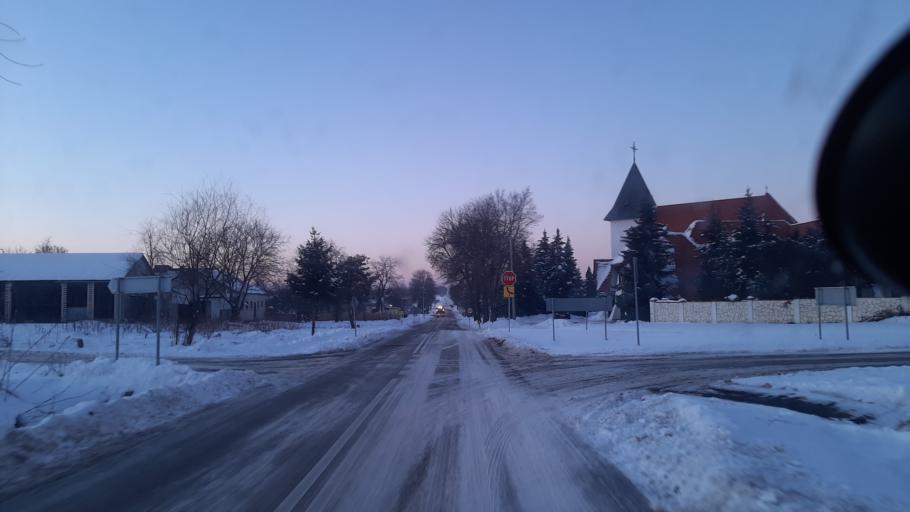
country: PL
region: Lublin Voivodeship
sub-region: Powiat lubelski
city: Niemce
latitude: 51.3598
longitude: 22.5319
